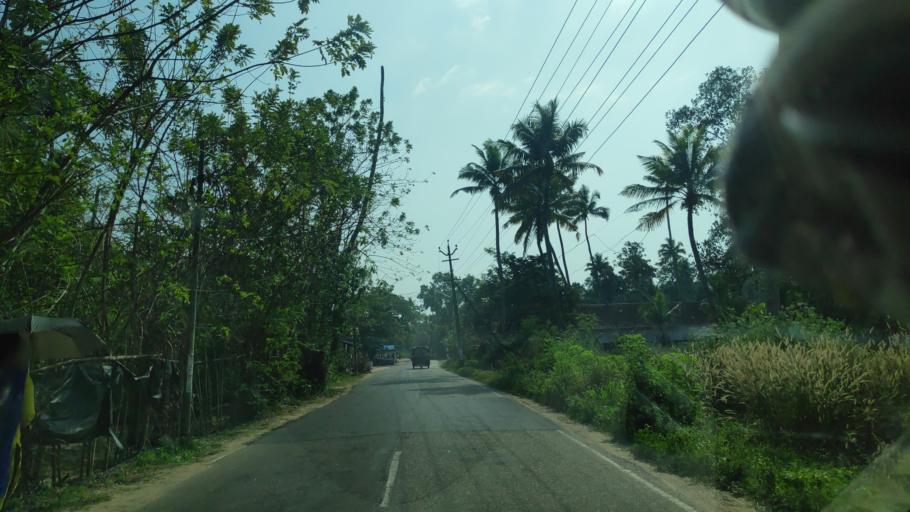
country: IN
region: Kerala
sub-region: Alappuzha
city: Shertallai
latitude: 9.6226
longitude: 76.3006
